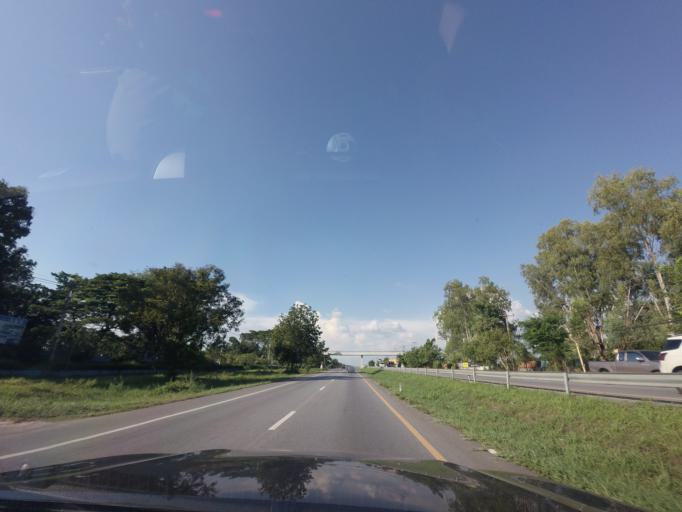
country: TH
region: Khon Kaen
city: Non Sila
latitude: 15.9758
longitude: 102.6943
